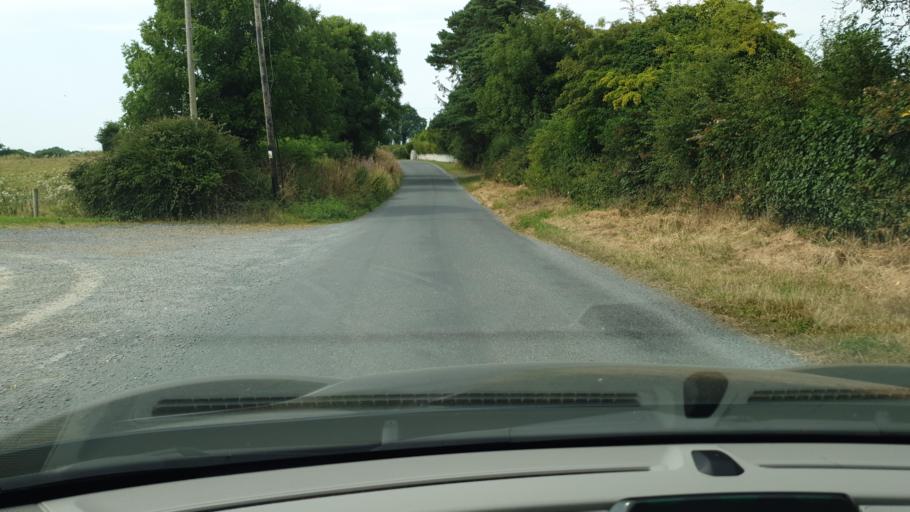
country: IE
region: Leinster
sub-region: An Mhi
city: Athboy
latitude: 53.6662
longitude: -6.9249
